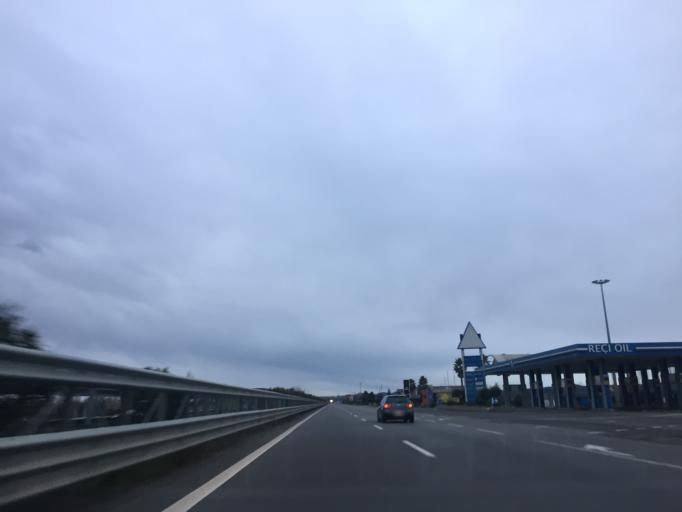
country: AL
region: Durres
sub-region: Rrethi i Krujes
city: Thumane
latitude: 41.5656
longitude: 19.6740
